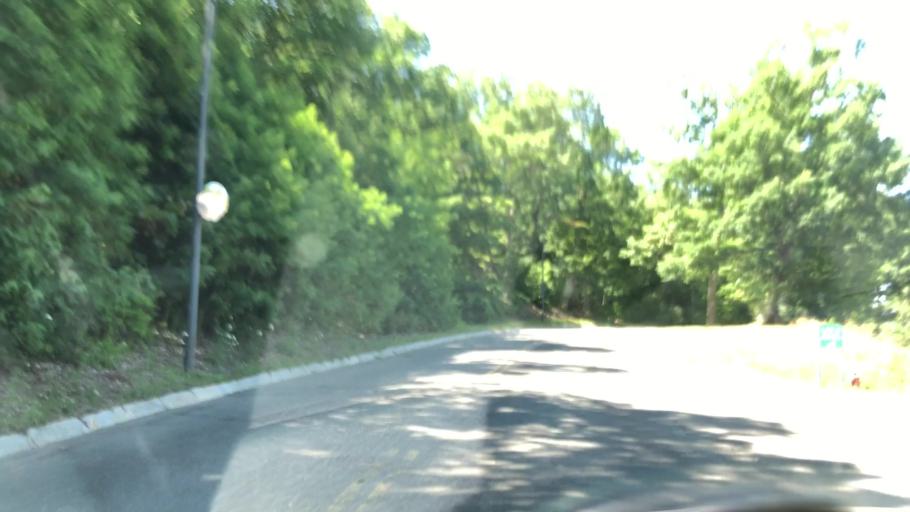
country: US
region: Massachusetts
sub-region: Hampden County
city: Holyoke
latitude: 42.1938
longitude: -72.6536
